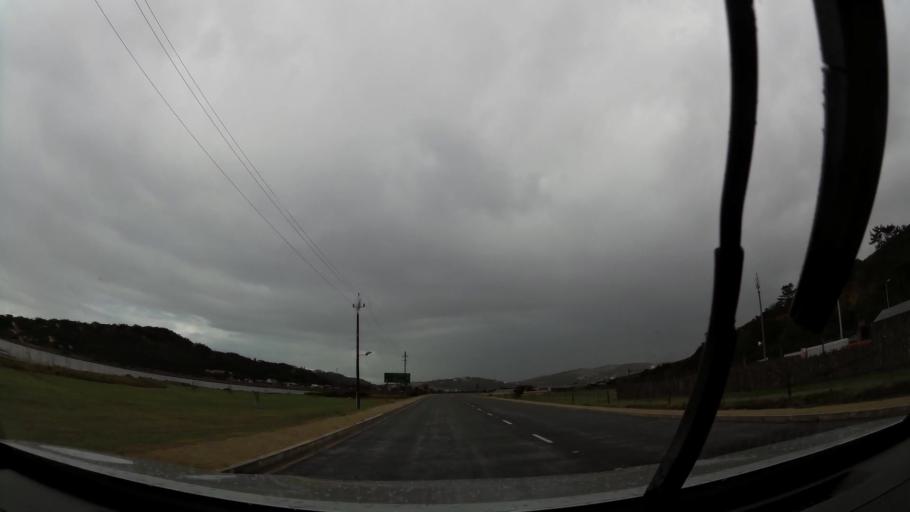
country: ZA
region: Western Cape
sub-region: Eden District Municipality
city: Mossel Bay
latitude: -34.0511
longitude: 22.2342
